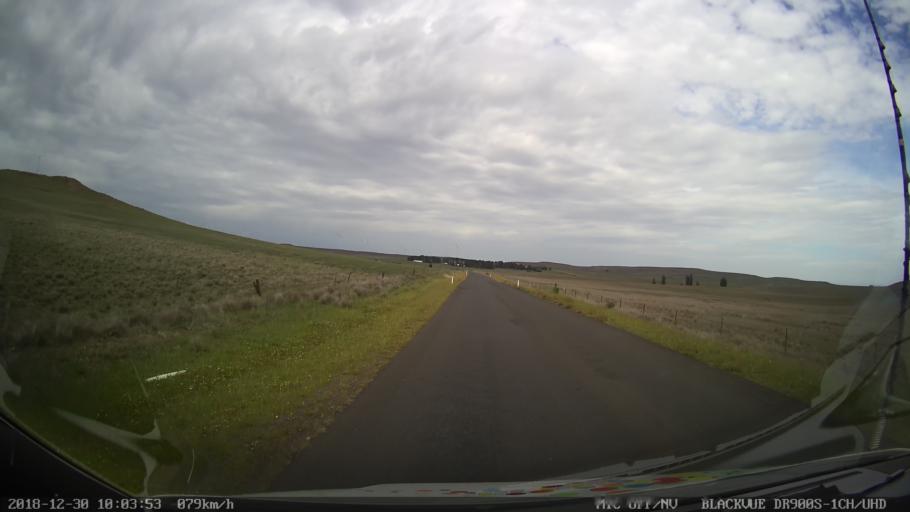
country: AU
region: New South Wales
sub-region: Cooma-Monaro
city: Cooma
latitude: -36.5172
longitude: 149.1519
